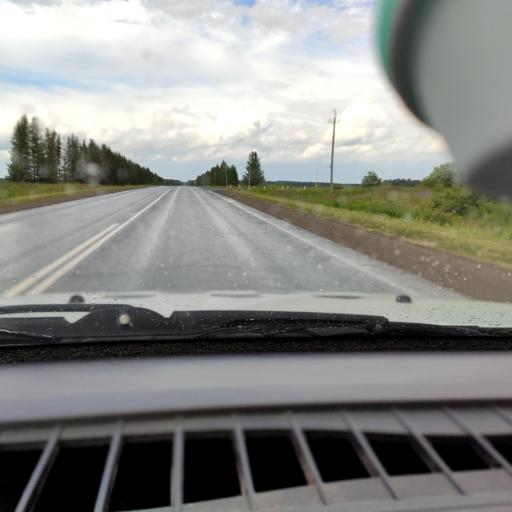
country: RU
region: Perm
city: Orda
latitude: 57.2072
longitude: 56.9287
